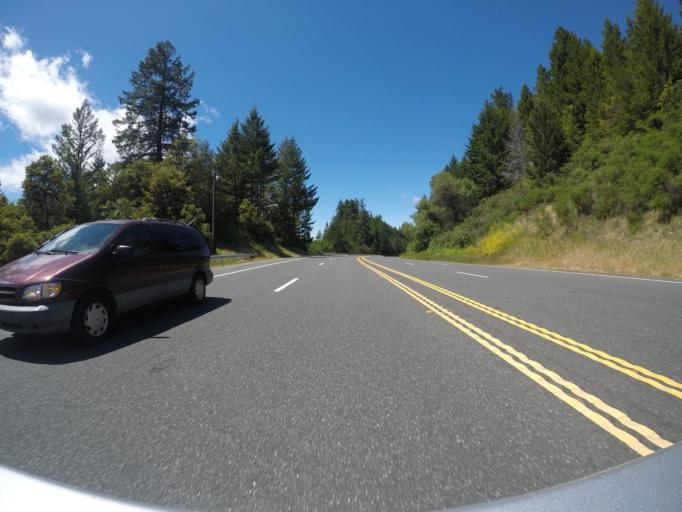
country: US
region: California
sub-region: Humboldt County
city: Redway
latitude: 39.9393
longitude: -123.7765
